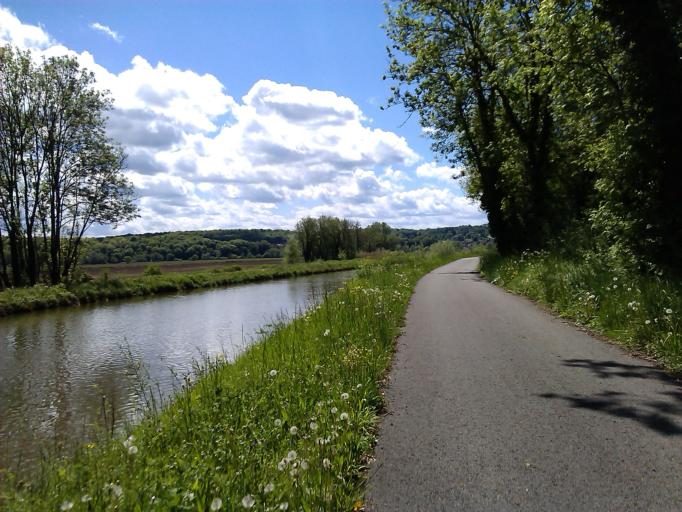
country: FR
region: Franche-Comte
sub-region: Territoire de Belfort
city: Mezire
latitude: 47.5381
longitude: 6.9102
